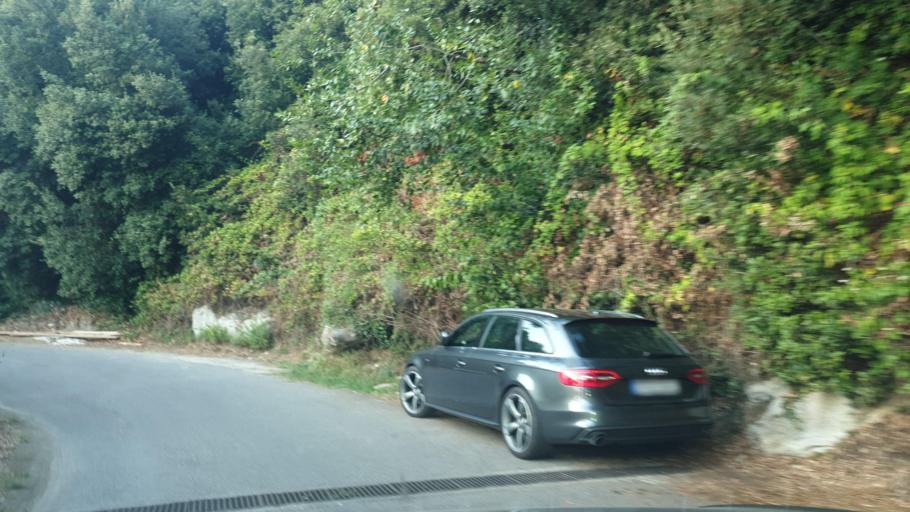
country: IT
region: Liguria
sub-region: Provincia di La Spezia
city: Bonassola
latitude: 44.1901
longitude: 9.5858
